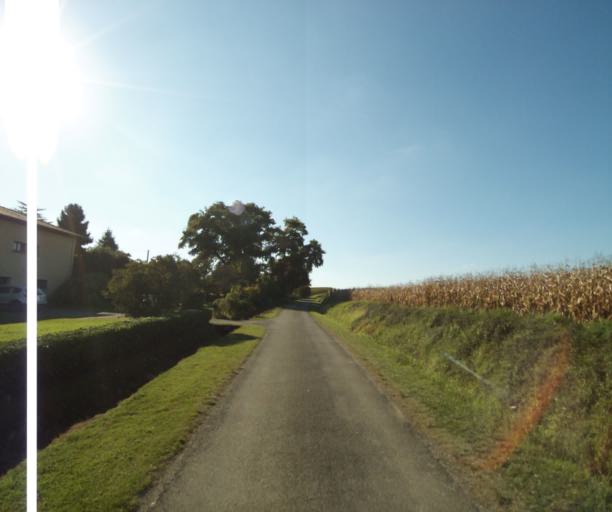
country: FR
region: Midi-Pyrenees
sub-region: Departement du Gers
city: Eauze
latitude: 43.8078
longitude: 0.1466
